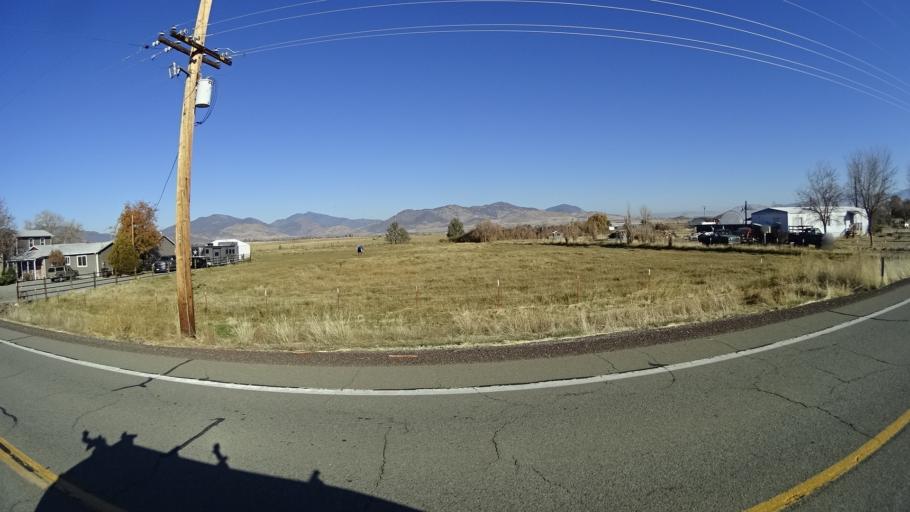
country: US
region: California
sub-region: Siskiyou County
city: Montague
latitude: 41.7057
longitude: -122.5623
